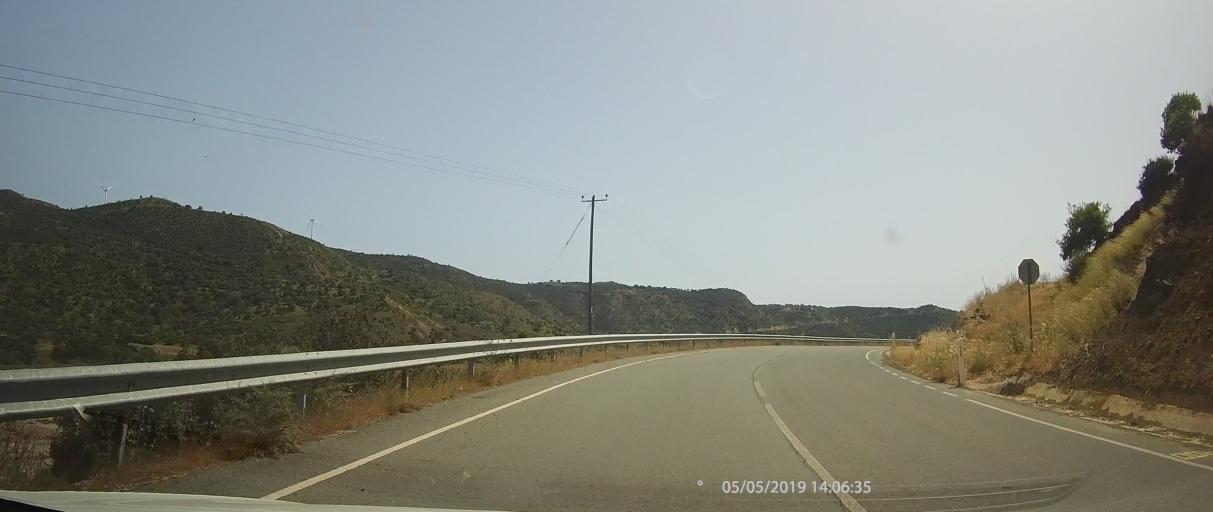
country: CY
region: Limassol
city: Pissouri
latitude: 34.7426
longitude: 32.6049
